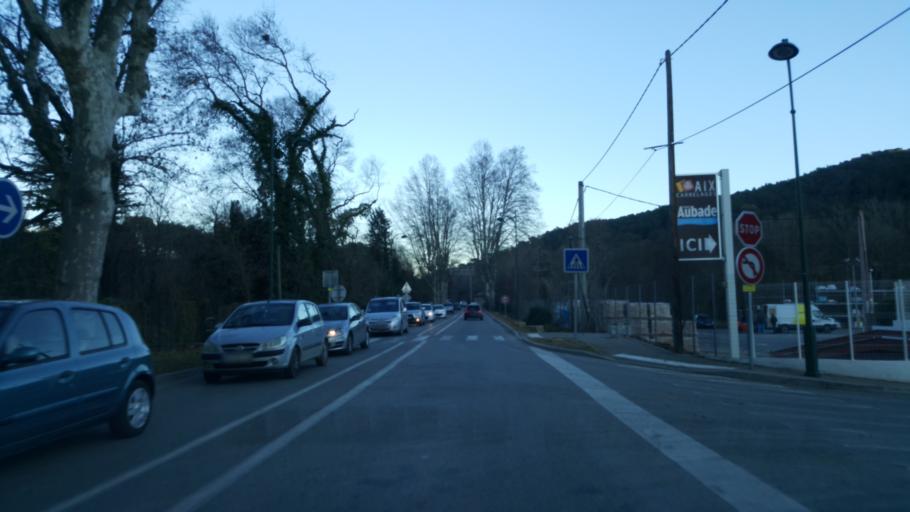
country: FR
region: Provence-Alpes-Cote d'Azur
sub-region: Departement des Bouches-du-Rhone
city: Meyreuil
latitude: 43.5086
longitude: 5.4932
